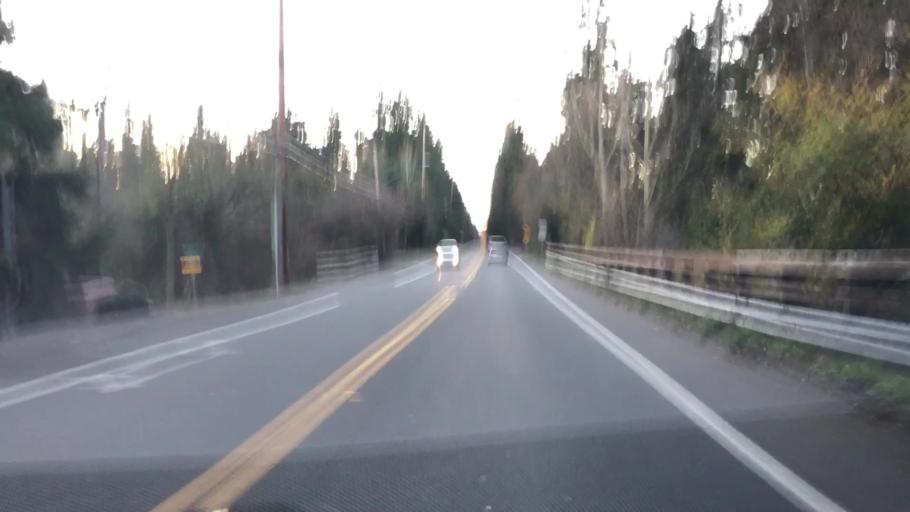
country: US
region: Washington
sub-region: King County
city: Yarrow Point
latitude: 47.6459
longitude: -122.1855
